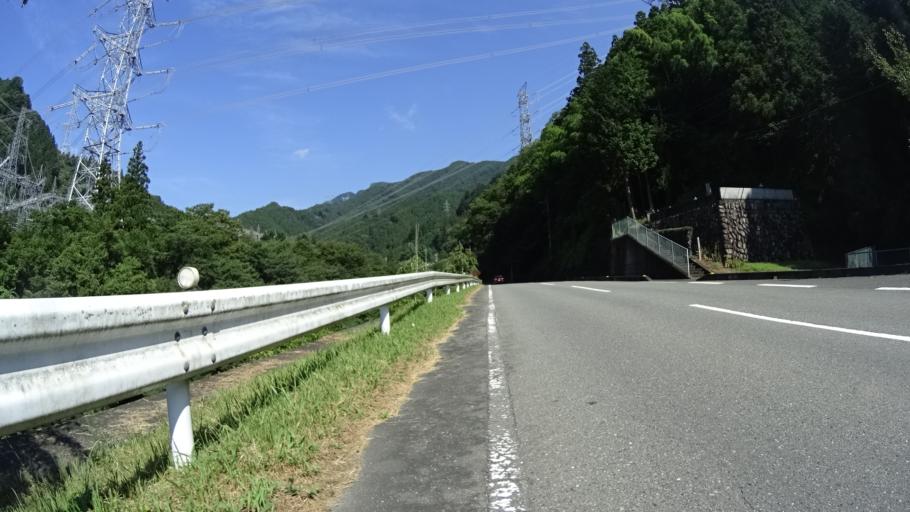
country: JP
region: Saitama
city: Chichibu
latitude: 36.0306
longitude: 138.9393
